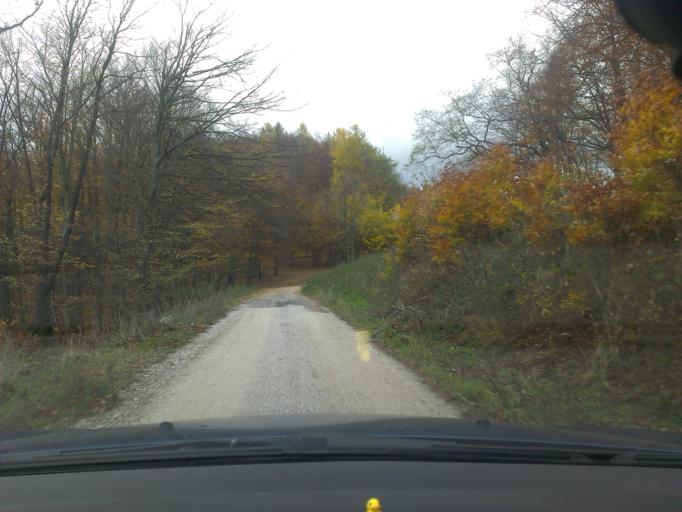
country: SK
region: Trnavsky
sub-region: Okres Trnava
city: Piestany
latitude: 48.6159
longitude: 17.9579
